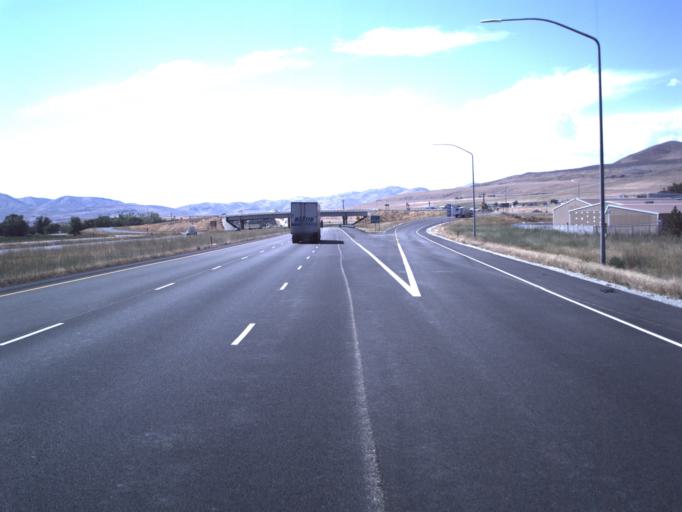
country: US
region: Utah
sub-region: Box Elder County
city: Tremonton
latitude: 41.7087
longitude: -112.2009
